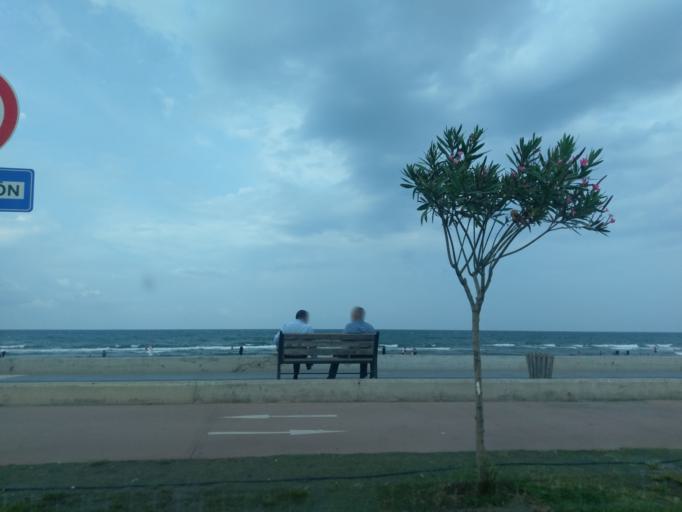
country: TR
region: Samsun
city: Samsun
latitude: 41.3318
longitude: 36.2901
